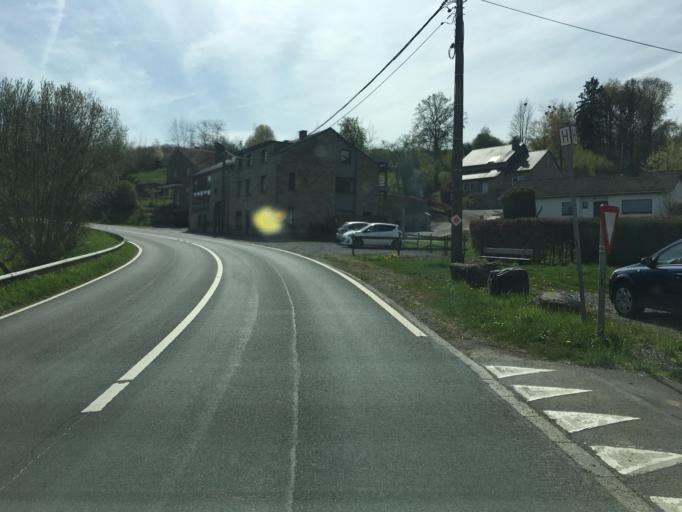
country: BE
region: Wallonia
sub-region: Province de Liege
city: Aywaille
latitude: 50.4331
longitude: 5.6653
